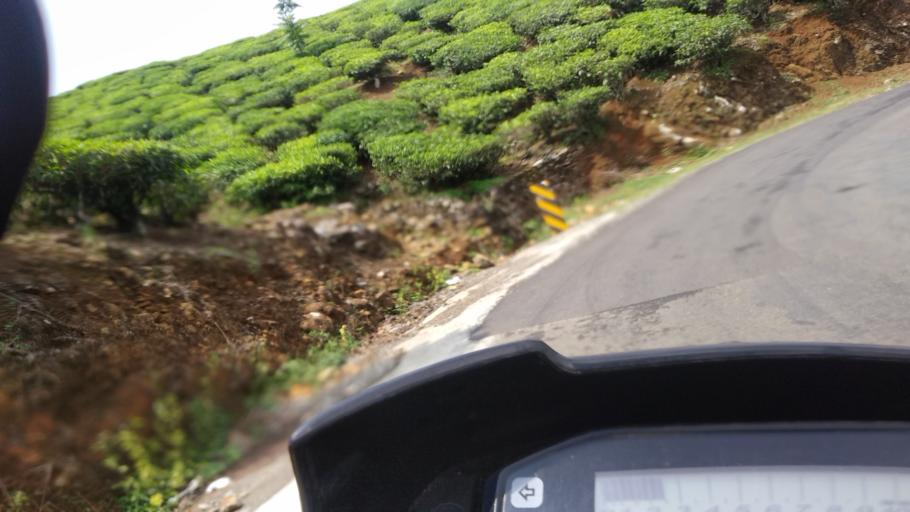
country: IN
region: Kerala
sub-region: Kottayam
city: Erattupetta
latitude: 9.6255
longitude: 76.9712
